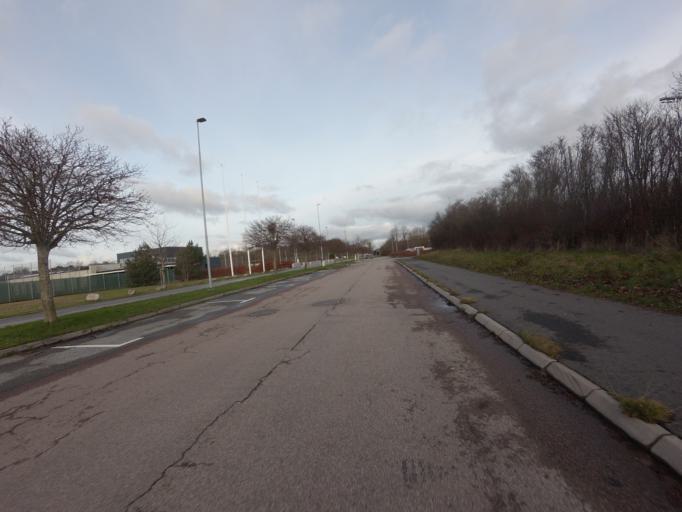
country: SE
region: Skane
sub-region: Hoganas Kommun
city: Hoganas
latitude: 56.1831
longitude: 12.5671
